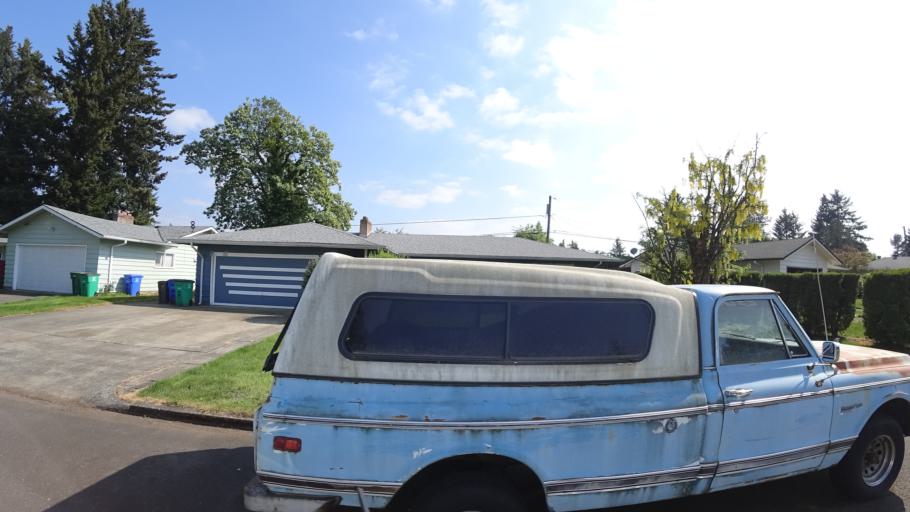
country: US
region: Oregon
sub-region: Multnomah County
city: Fairview
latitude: 45.5165
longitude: -122.4949
